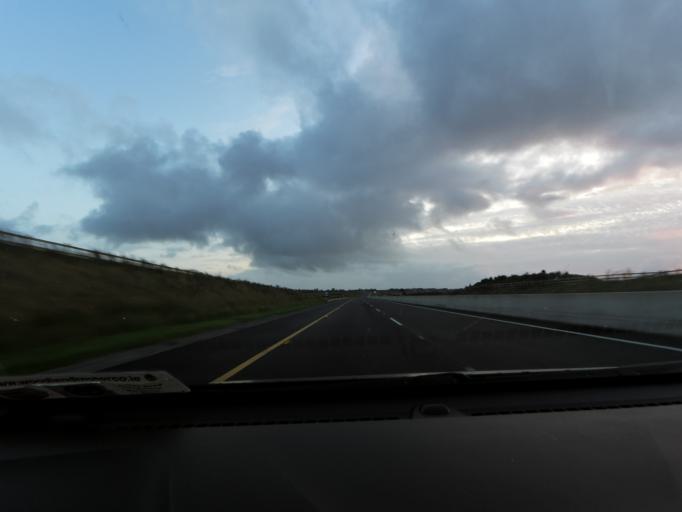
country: IE
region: Connaught
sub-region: County Galway
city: Athenry
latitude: 53.3583
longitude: -8.7910
